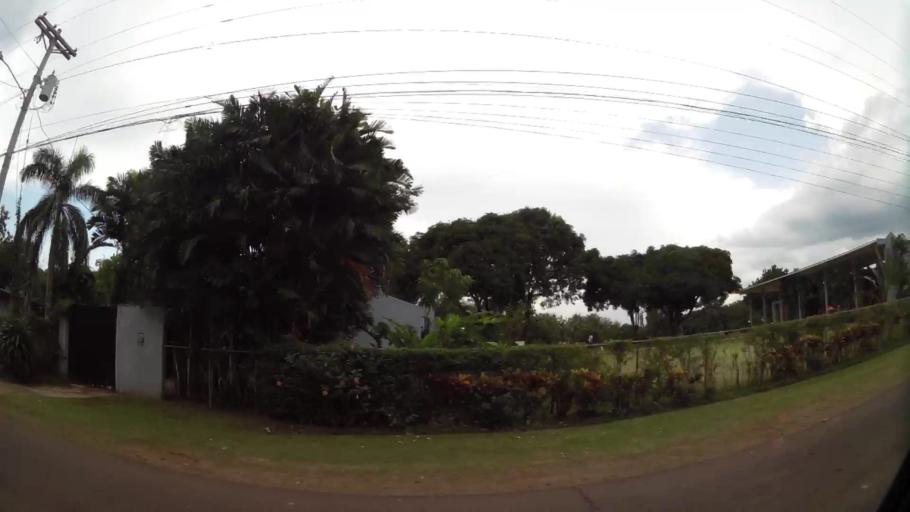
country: PA
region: Panama
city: Cabra Numero Uno
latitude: 9.1216
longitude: -79.3599
